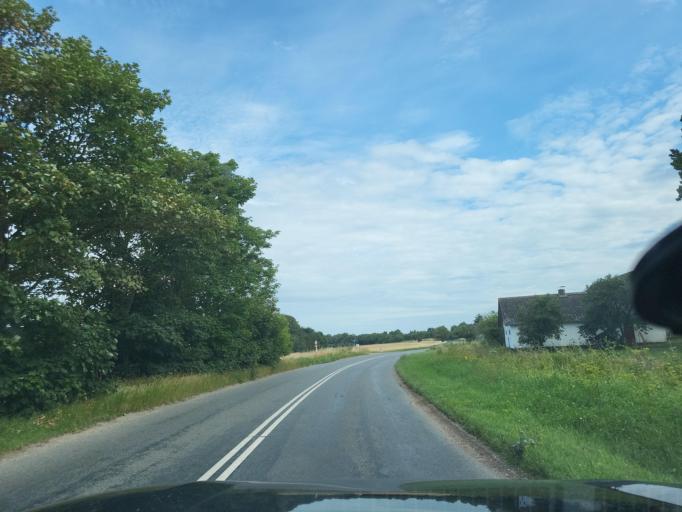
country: DK
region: Zealand
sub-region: Kalundborg Kommune
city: Svebolle
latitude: 55.7431
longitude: 11.3406
